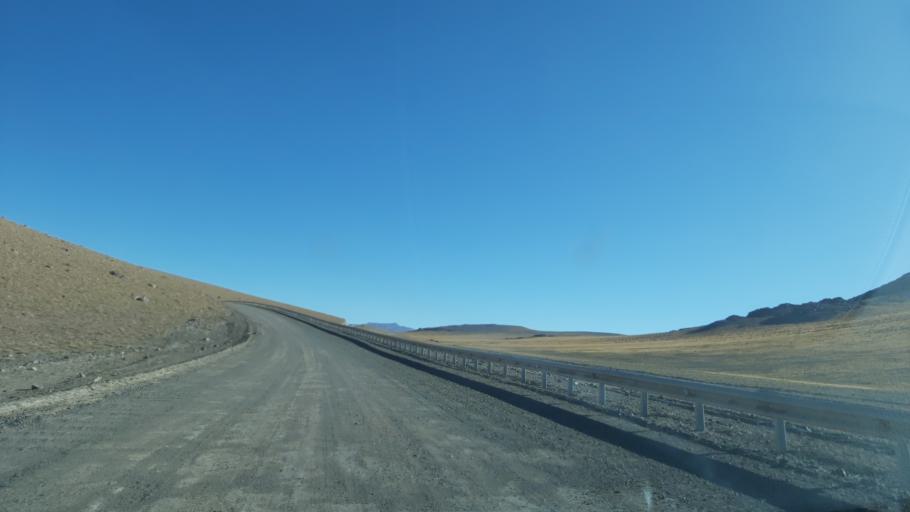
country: CL
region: Atacama
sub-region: Provincia de Chanaral
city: Diego de Almagro
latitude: -26.4441
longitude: -69.2873
